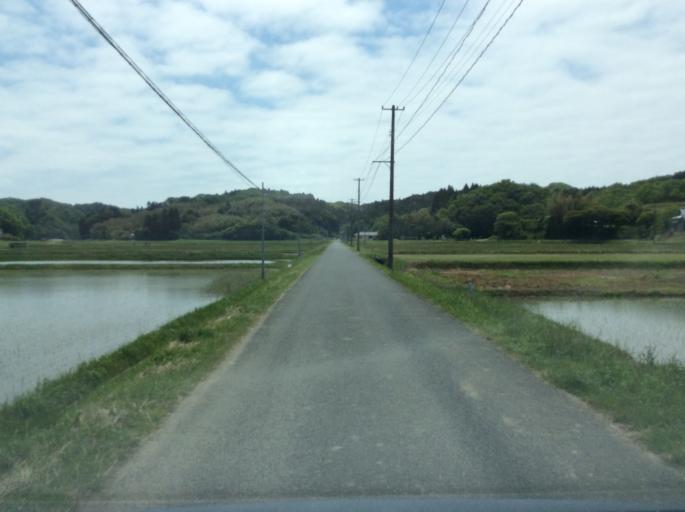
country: JP
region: Fukushima
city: Iwaki
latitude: 37.0169
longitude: 140.9395
